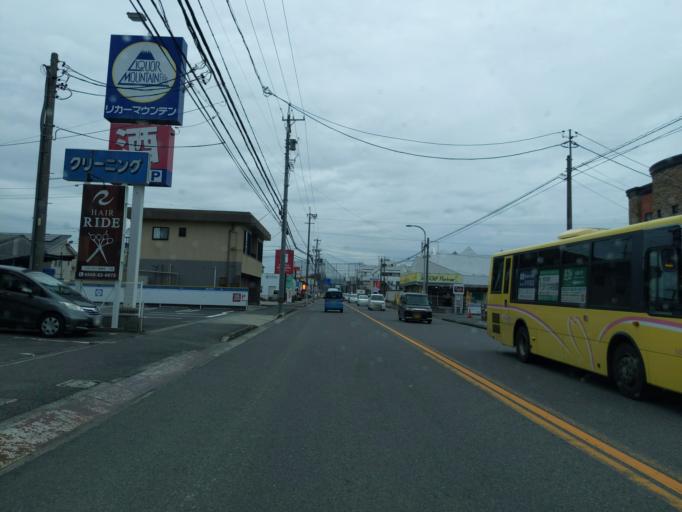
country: JP
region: Aichi
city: Kasugai
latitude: 35.2675
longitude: 136.9838
